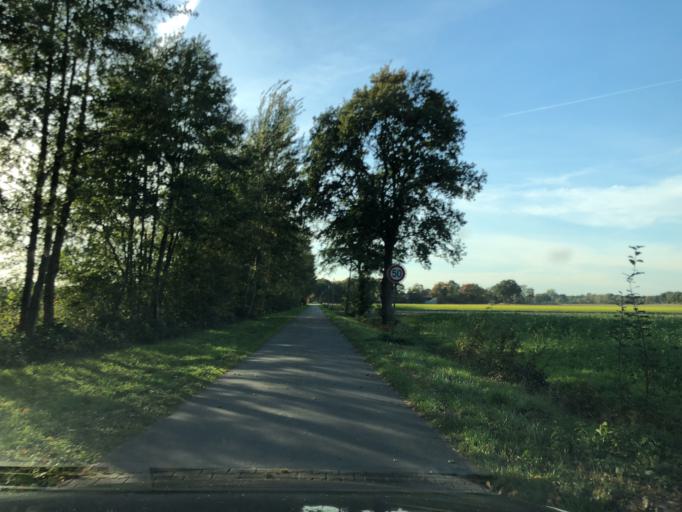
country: DE
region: Lower Saxony
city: Neulehe
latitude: 53.0307
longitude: 7.3674
